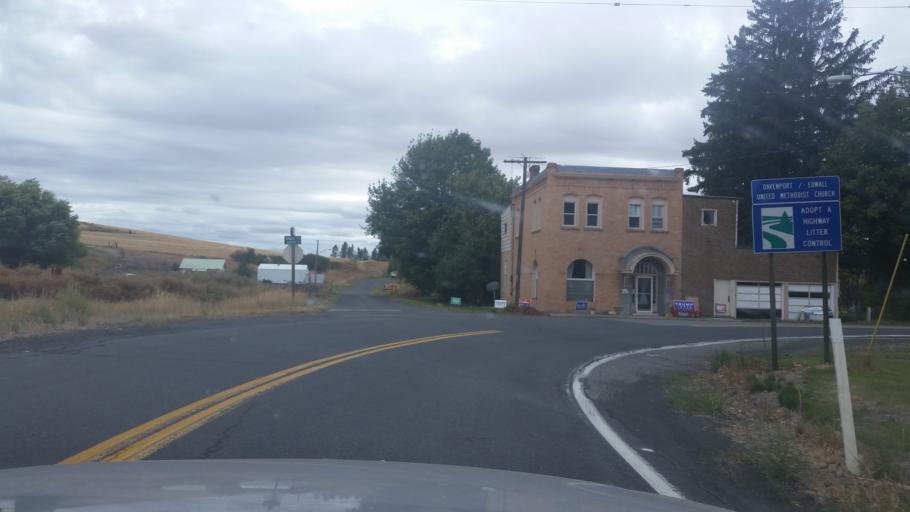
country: US
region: Washington
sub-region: Lincoln County
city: Davenport
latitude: 47.5060
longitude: -117.9495
